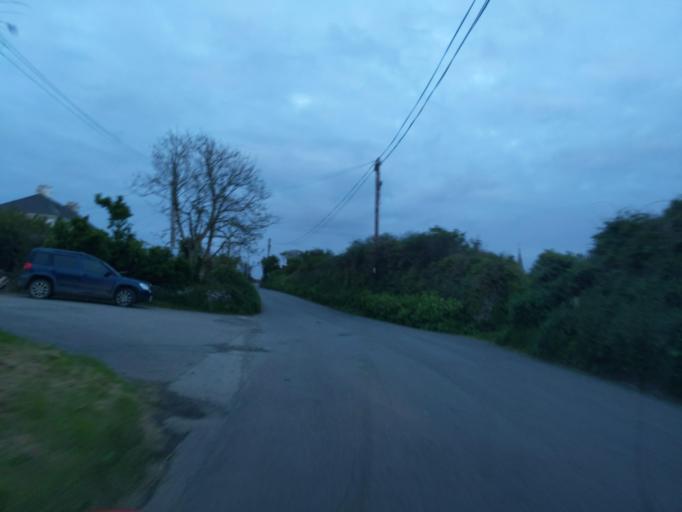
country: GB
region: England
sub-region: Cornwall
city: Polzeath
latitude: 50.5591
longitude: -4.8778
